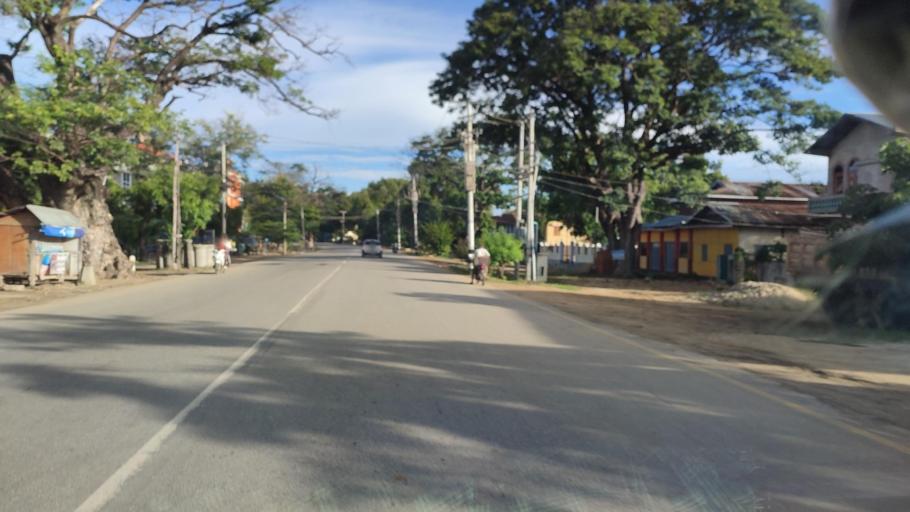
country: MM
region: Mandalay
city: Yamethin
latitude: 20.1372
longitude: 96.1975
